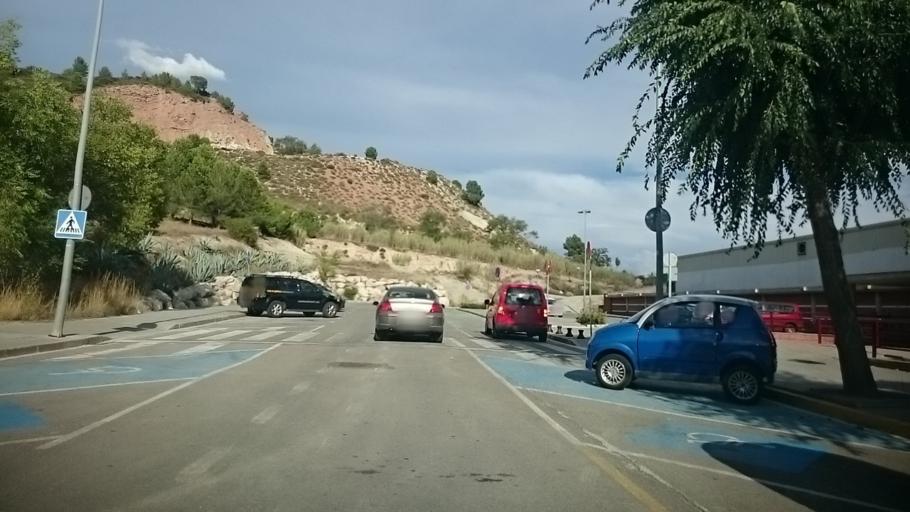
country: ES
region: Catalonia
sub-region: Provincia de Barcelona
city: Igualada
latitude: 41.5961
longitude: 1.6226
